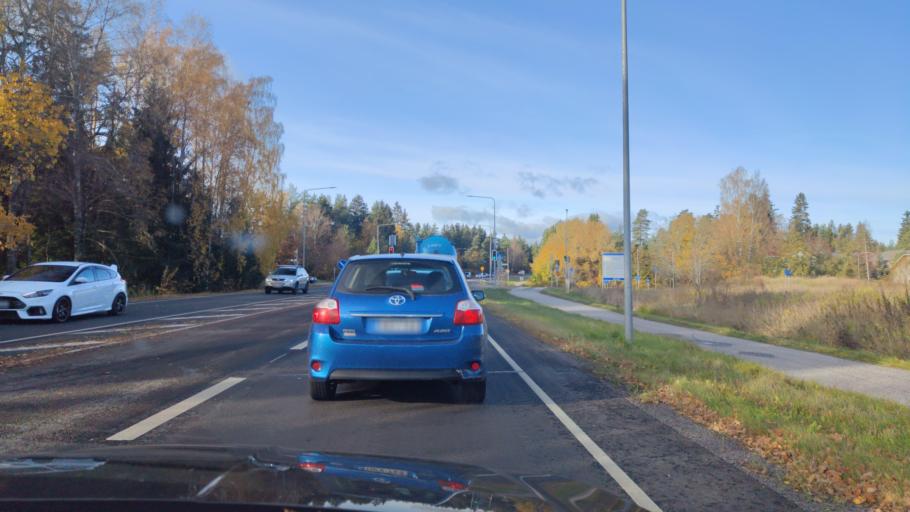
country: FI
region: Varsinais-Suomi
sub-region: Turku
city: Kaarina
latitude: 60.4454
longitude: 22.3765
